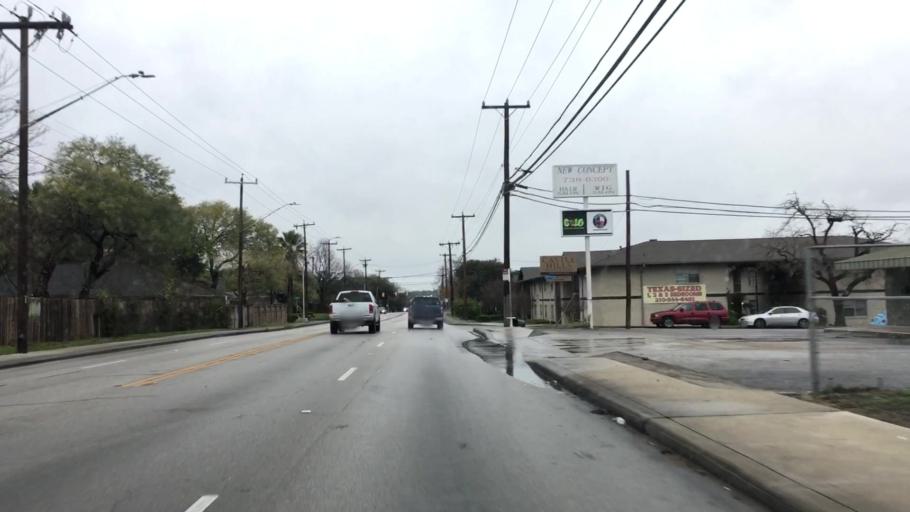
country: US
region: Texas
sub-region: Bexar County
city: Castle Hills
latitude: 29.5102
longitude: -98.5068
